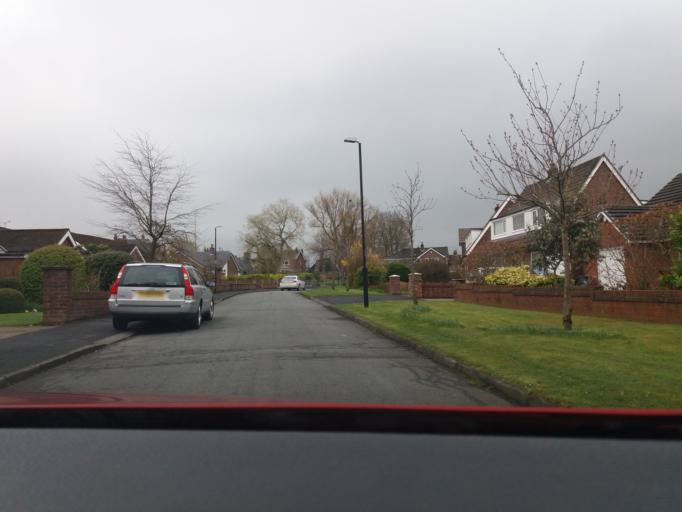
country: GB
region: England
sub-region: Lancashire
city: Chorley
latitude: 53.6559
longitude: -2.6413
